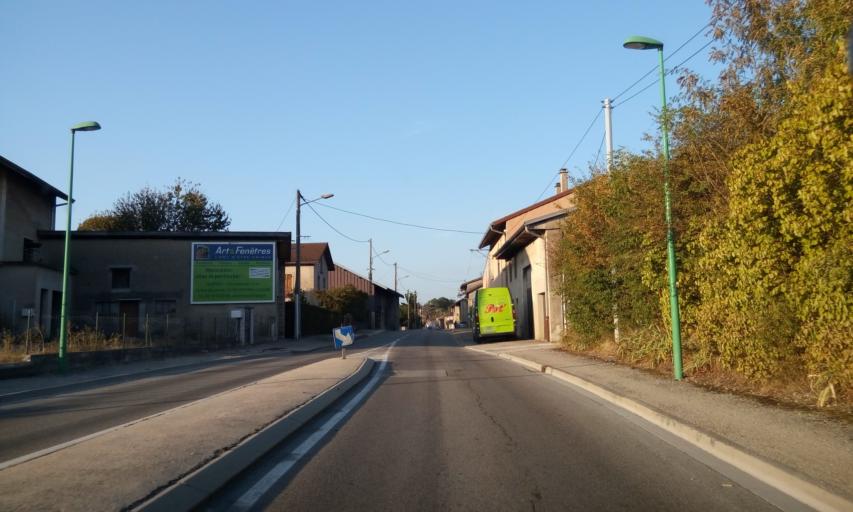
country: FR
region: Rhone-Alpes
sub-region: Departement de l'Ain
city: Saint-Martin-du-Frene
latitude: 46.1348
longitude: 5.5500
